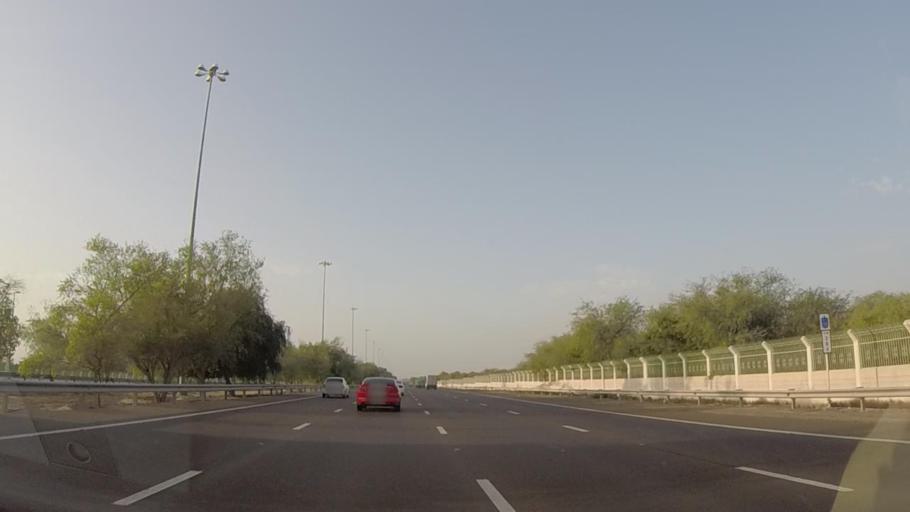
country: AE
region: Dubai
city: Dubai
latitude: 24.8264
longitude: 54.8798
